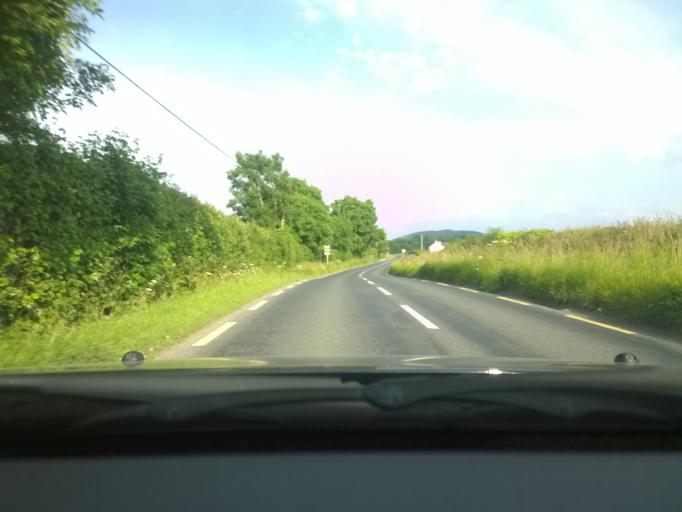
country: IE
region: Leinster
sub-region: Kildare
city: Rathangan
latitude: 53.2156
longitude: -6.9740
